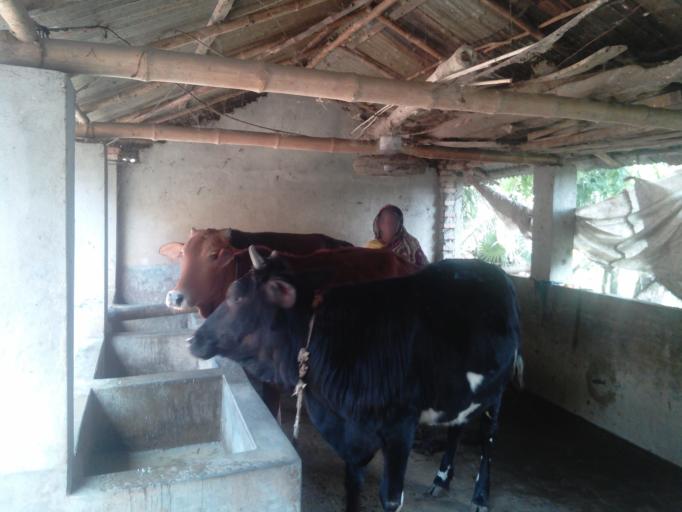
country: BD
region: Khulna
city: Kesabpur
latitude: 22.7828
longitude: 89.2810
